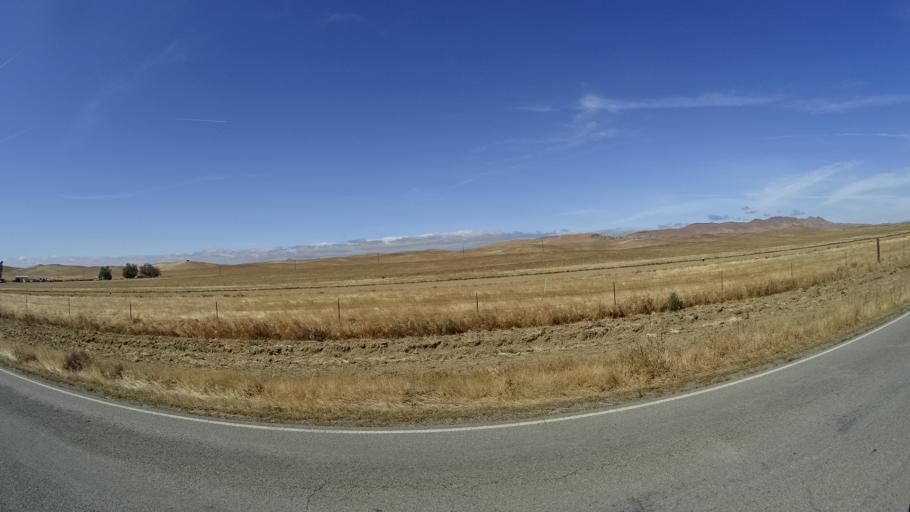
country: US
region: California
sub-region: Kings County
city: Avenal
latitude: 35.9091
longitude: -120.0628
